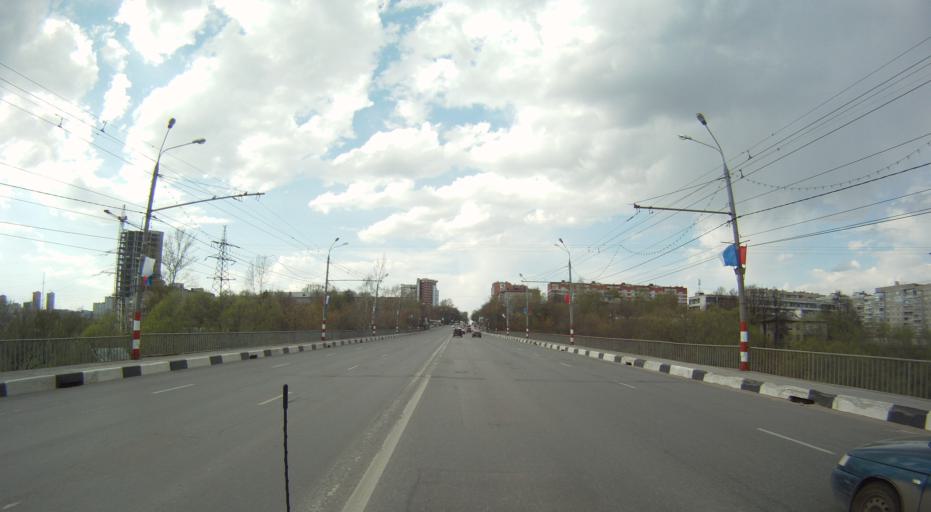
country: RU
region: Nizjnij Novgorod
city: Nizhniy Novgorod
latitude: 56.3058
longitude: 44.0259
